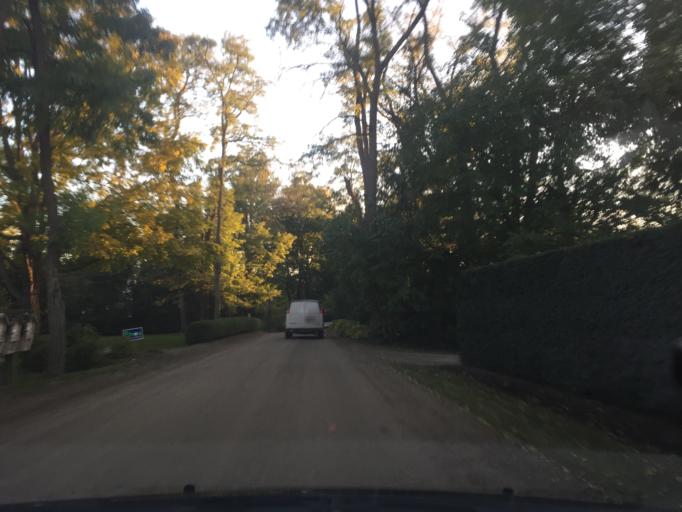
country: US
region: Michigan
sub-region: Oakland County
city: Franklin
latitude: 42.5510
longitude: -83.2937
